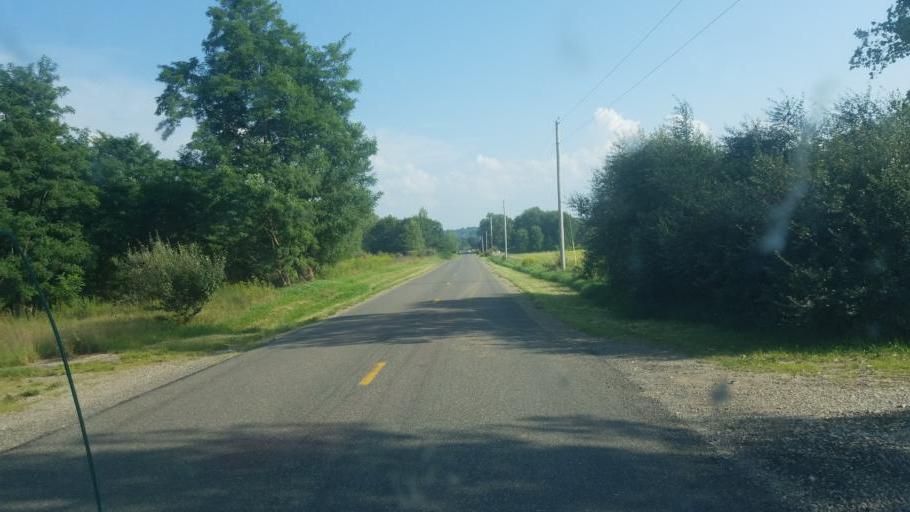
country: US
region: Ohio
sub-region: Medina County
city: Westfield Center
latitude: 41.0024
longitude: -81.9611
